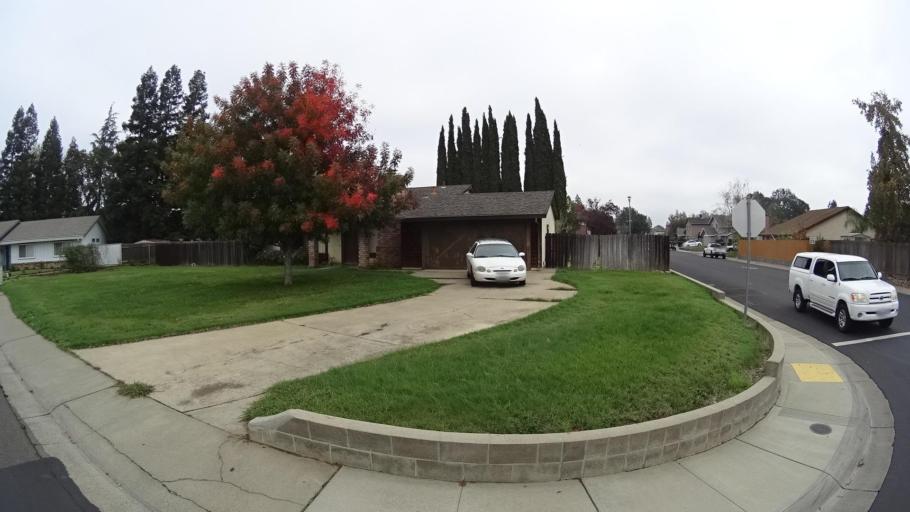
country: US
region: California
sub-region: Sacramento County
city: Elk Grove
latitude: 38.3978
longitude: -121.3674
